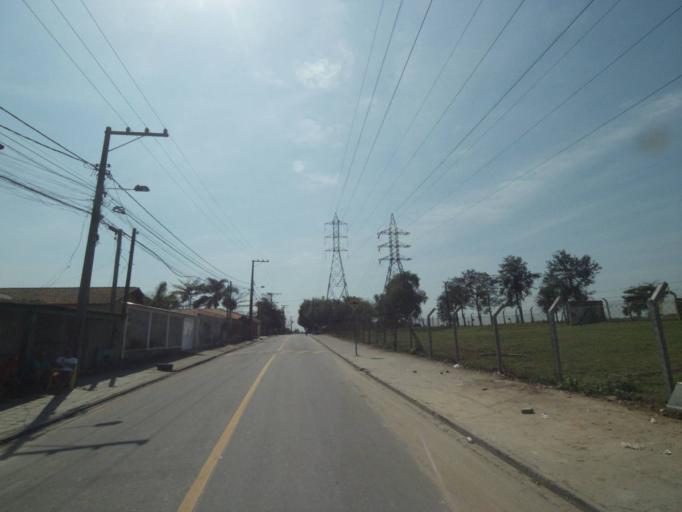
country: BR
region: Parana
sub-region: Paranagua
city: Paranagua
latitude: -25.5461
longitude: -48.5517
